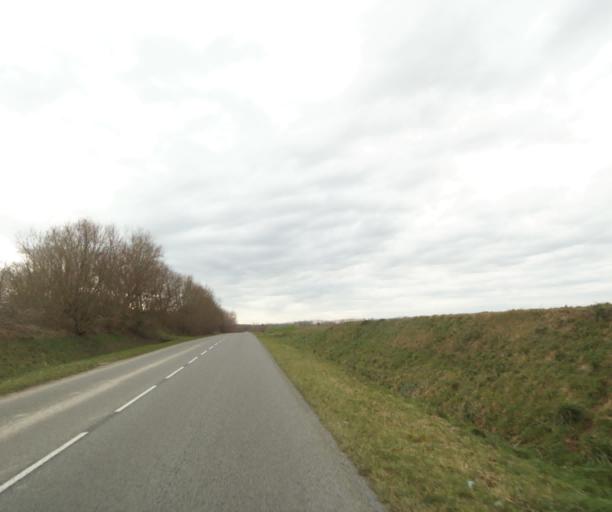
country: FR
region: Nord-Pas-de-Calais
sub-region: Departement du Nord
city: Sebourg
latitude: 50.3285
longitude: 3.6338
